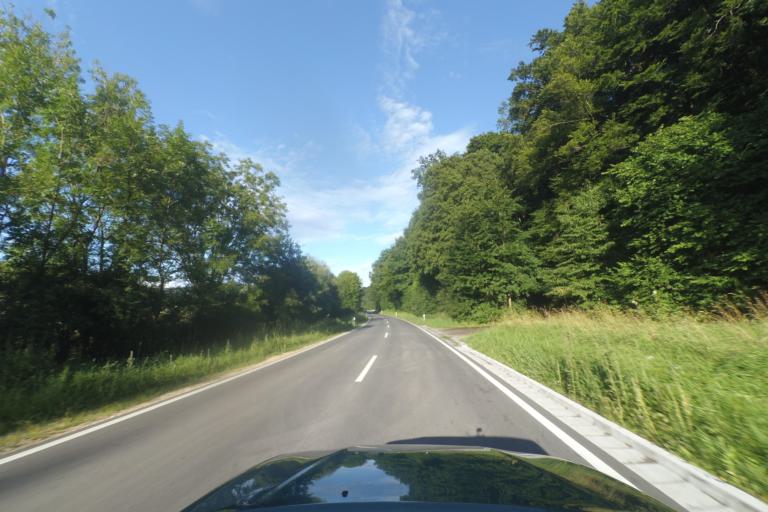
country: DE
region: Bavaria
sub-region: Upper Bavaria
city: Bohmfeld
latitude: 48.9198
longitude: 11.3596
